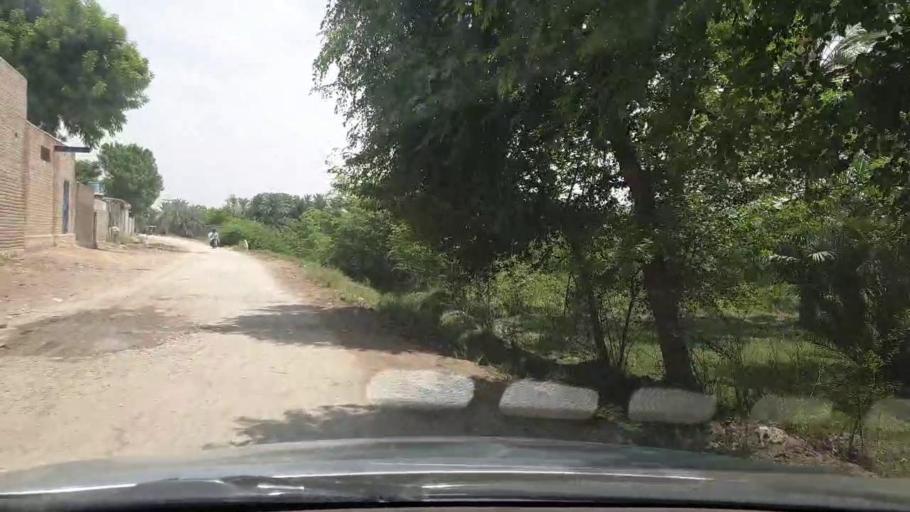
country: PK
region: Sindh
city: Khairpur
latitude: 27.4323
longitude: 68.7686
